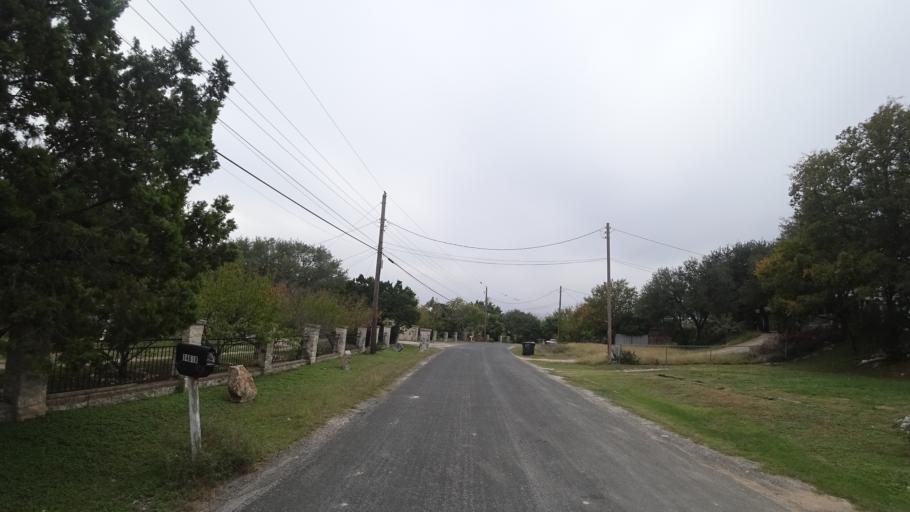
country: US
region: Texas
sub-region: Travis County
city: Hudson Bend
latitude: 30.3736
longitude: -97.9307
